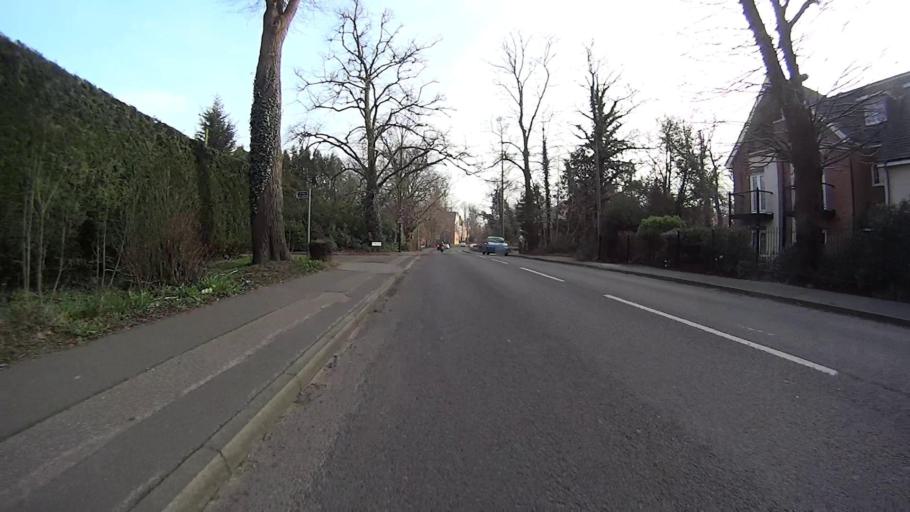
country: GB
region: England
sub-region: West Sussex
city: Maidenbower
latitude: 51.1141
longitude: -0.1469
